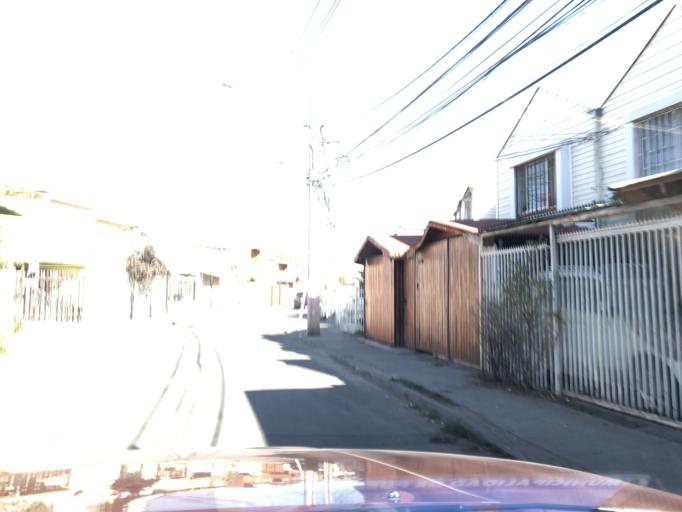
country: CL
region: Santiago Metropolitan
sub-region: Provincia de Cordillera
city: Puente Alto
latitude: -33.5934
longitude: -70.5600
